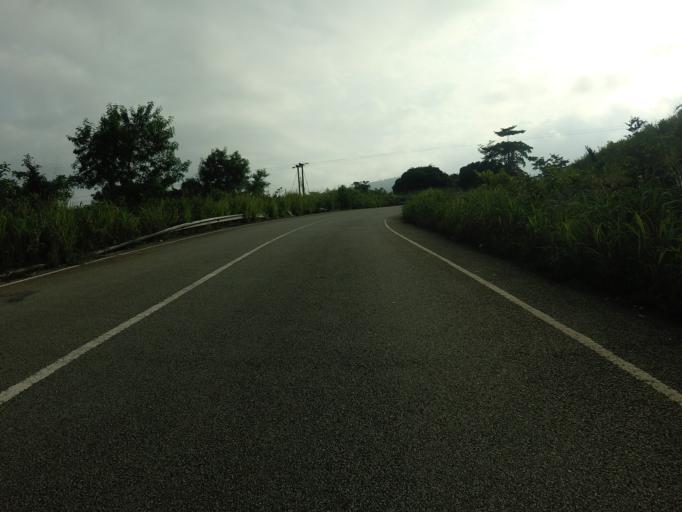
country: GH
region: Volta
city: Ho
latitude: 6.8110
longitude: 0.4215
